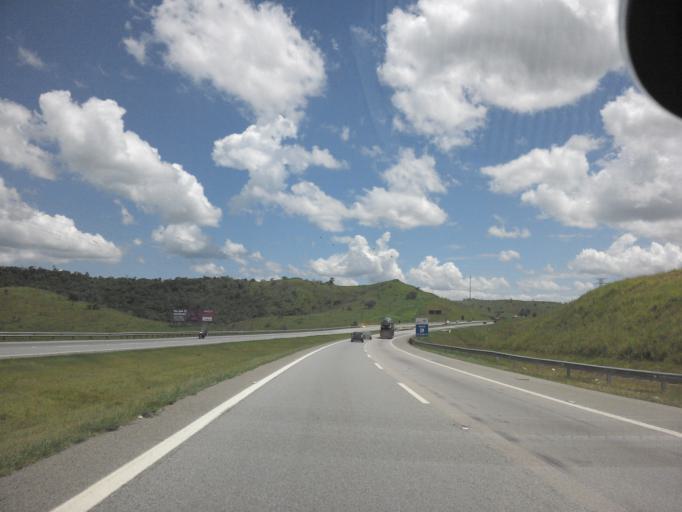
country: BR
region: Sao Paulo
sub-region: Jacarei
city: Jacarei
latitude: -23.3369
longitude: -45.9390
